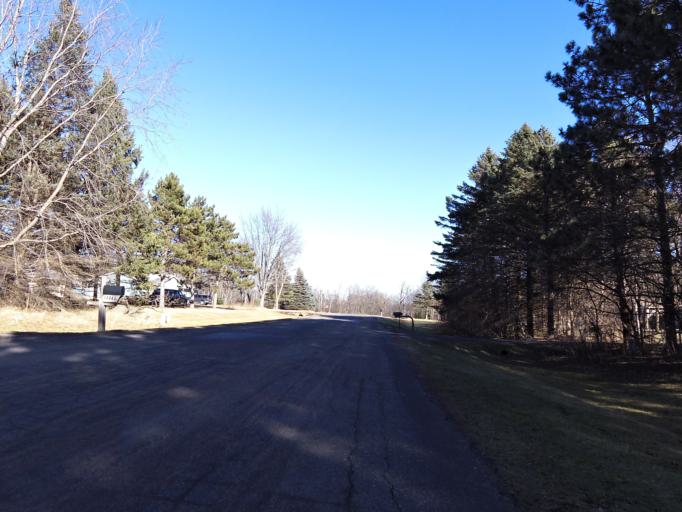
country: US
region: Minnesota
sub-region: Washington County
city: Bayport
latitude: 44.9829
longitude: -92.8214
